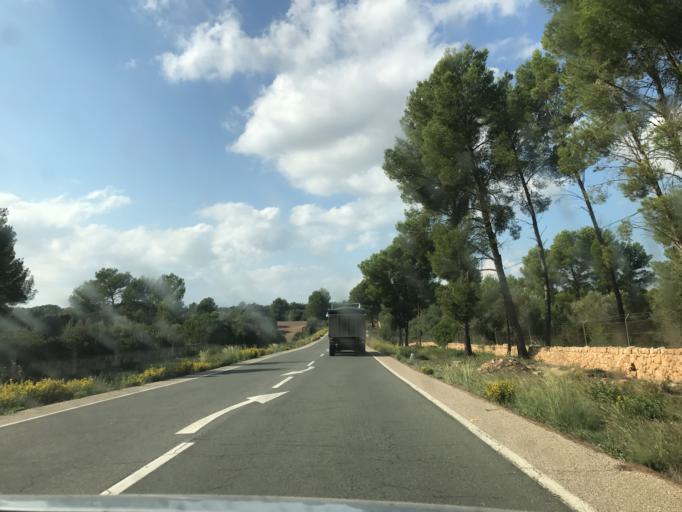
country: ES
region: Balearic Islands
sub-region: Illes Balears
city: Santa Margalida
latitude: 39.7253
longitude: 3.2061
